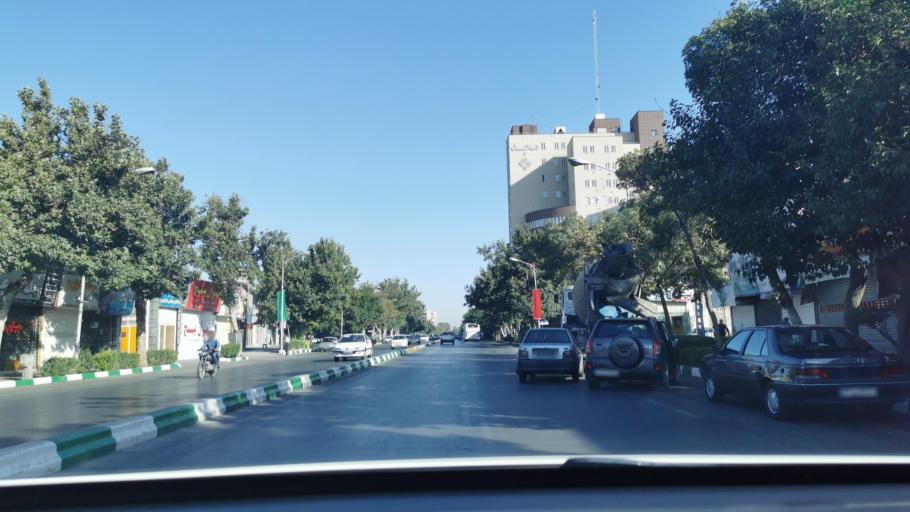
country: IR
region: Razavi Khorasan
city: Mashhad
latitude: 36.3108
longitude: 59.5922
